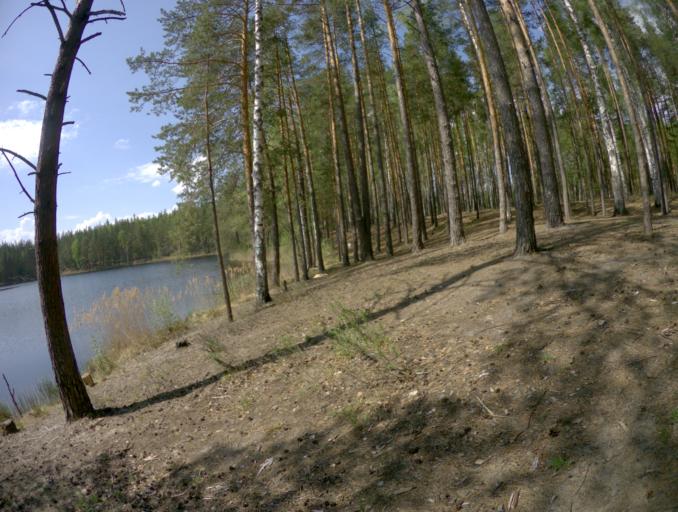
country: RU
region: Ivanovo
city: Talitsy
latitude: 56.4744
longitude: 42.1881
